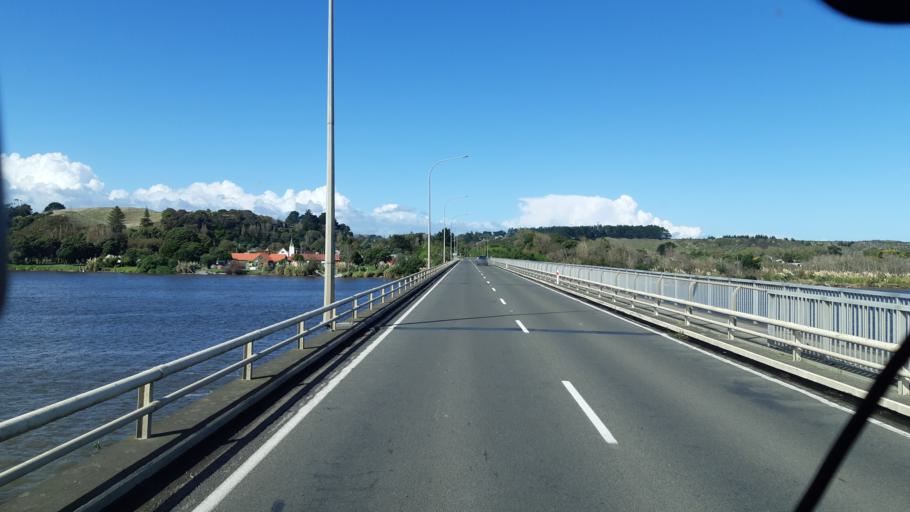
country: NZ
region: Manawatu-Wanganui
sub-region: Wanganui District
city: Wanganui
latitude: -39.9443
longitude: 175.0452
